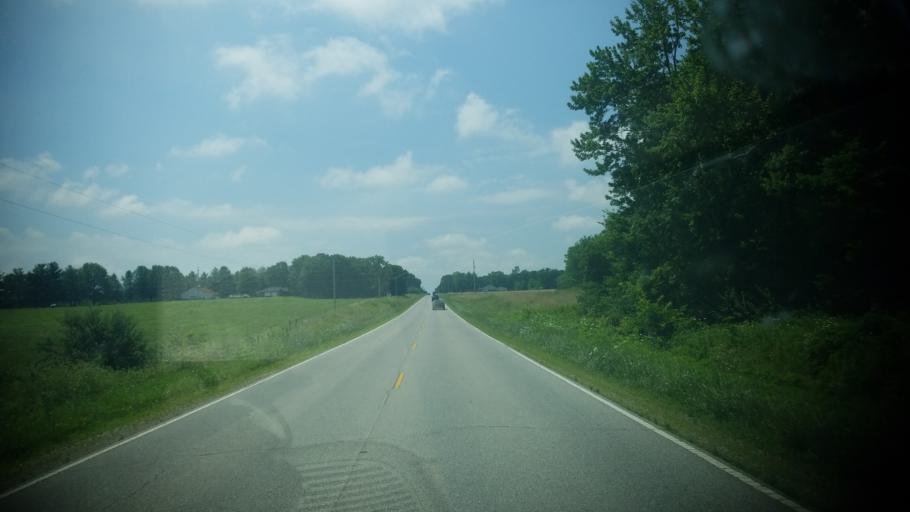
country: US
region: Illinois
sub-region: Wayne County
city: Fairfield
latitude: 38.4184
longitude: -88.3499
